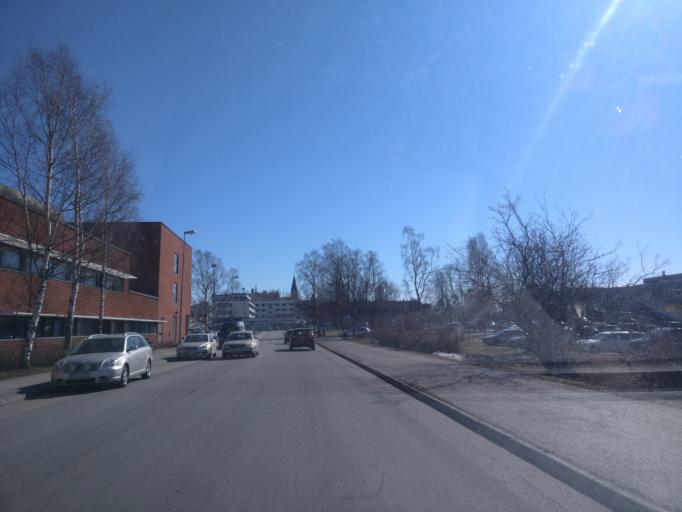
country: FI
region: Lapland
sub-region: Kemi-Tornio
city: Kemi
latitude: 65.7357
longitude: 24.5561
